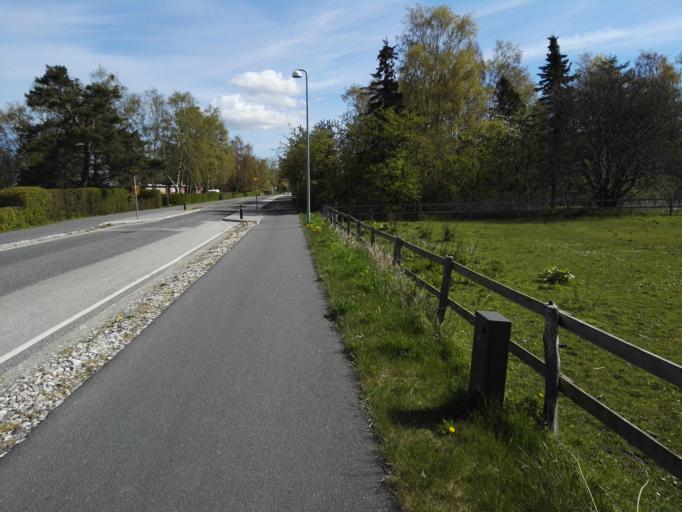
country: DK
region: Capital Region
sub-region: Halsnaes Kommune
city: Frederiksvaerk
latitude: 55.9716
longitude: 11.9953
